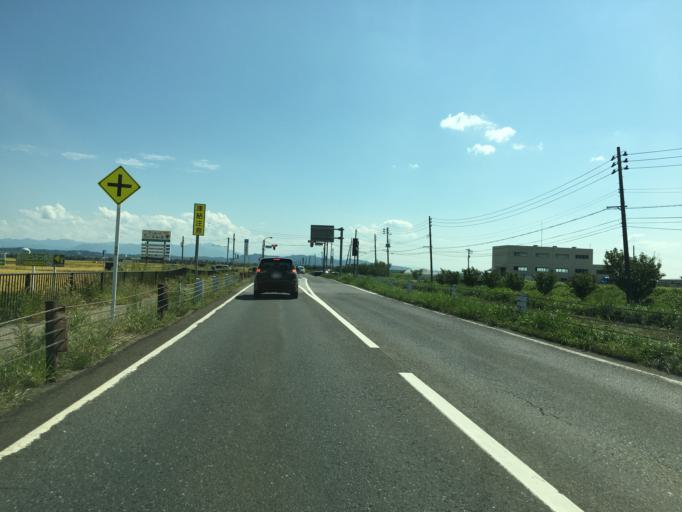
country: JP
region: Niigata
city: Kameda-honcho
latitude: 37.8331
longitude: 139.0968
